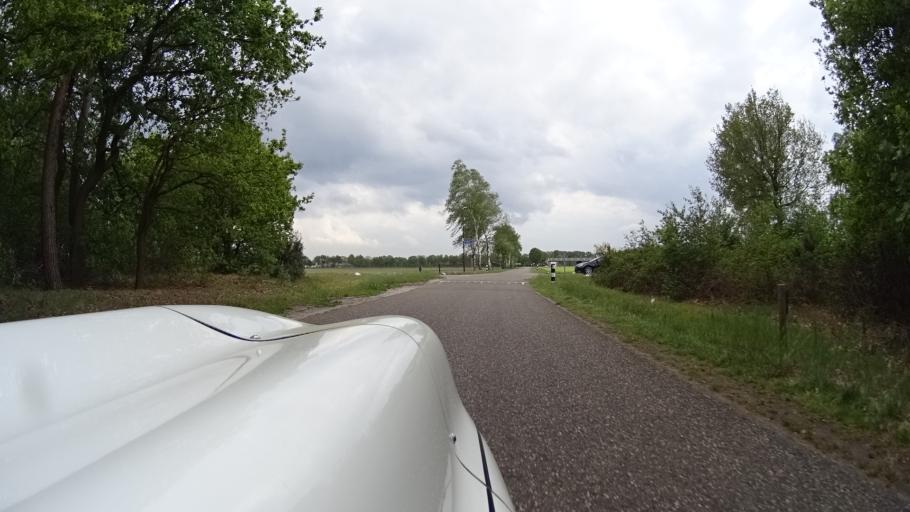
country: NL
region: North Brabant
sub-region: Gemeente Uden
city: Odiliapeel
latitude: 51.6311
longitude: 5.7072
